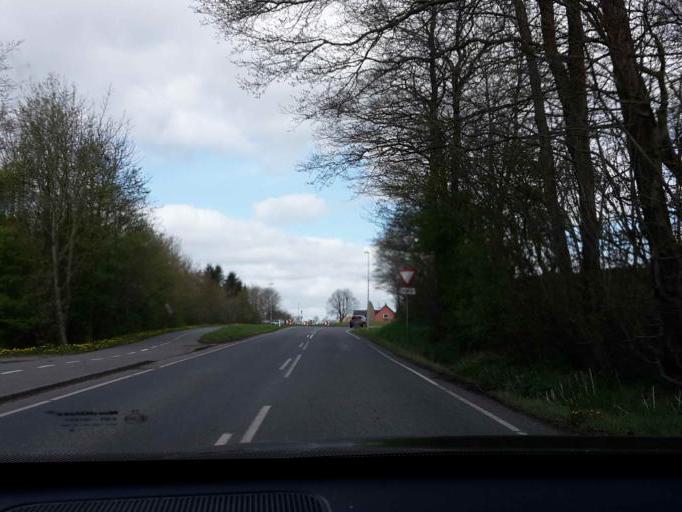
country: DK
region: South Denmark
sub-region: Varde Kommune
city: Olgod
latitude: 55.7254
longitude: 8.7253
